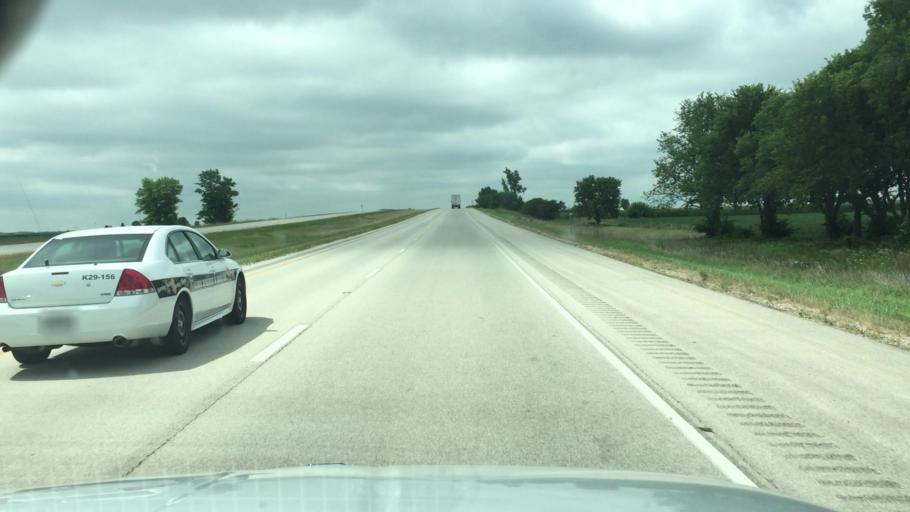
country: US
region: Illinois
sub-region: Henry County
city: Orion
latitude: 41.3554
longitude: -90.3316
